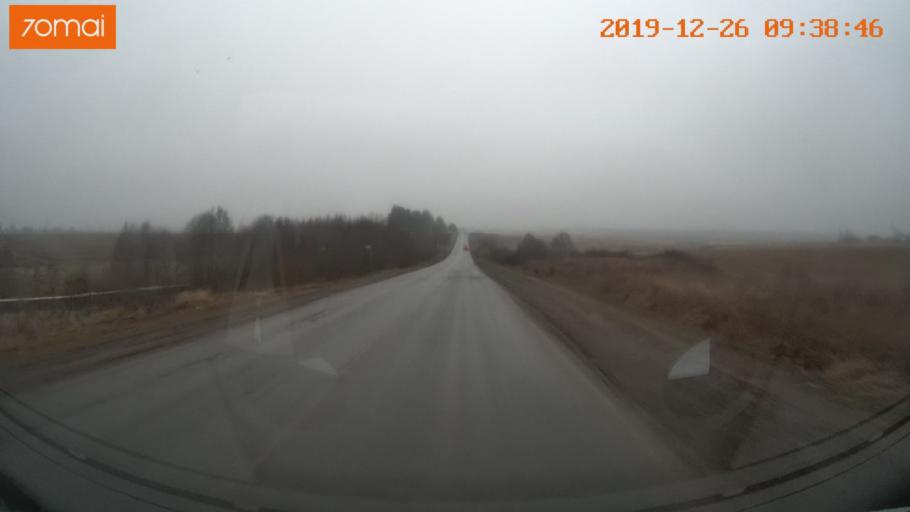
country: RU
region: Vologda
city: Vologda
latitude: 59.1476
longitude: 40.0367
